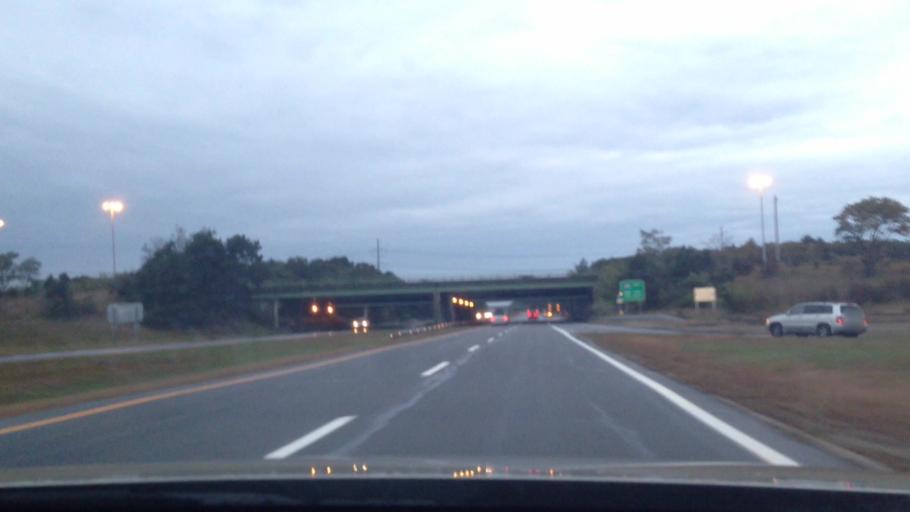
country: US
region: New York
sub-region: Suffolk County
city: Holtsville
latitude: 40.8185
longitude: -73.0539
